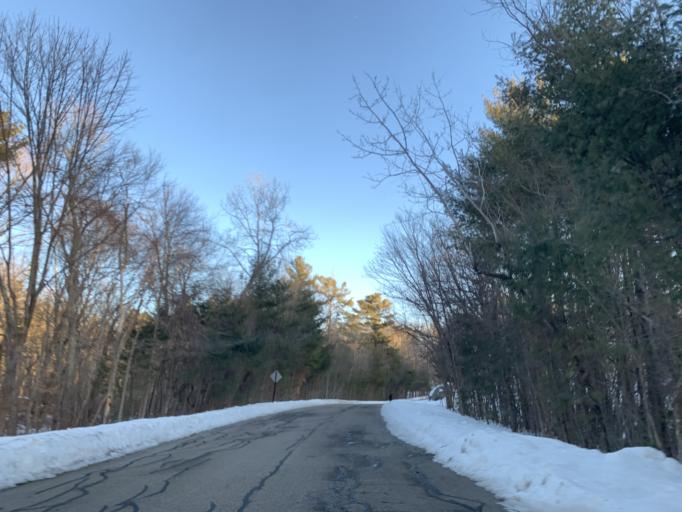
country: US
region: Massachusetts
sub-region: Norfolk County
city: Westwood
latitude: 42.2463
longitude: -71.2331
